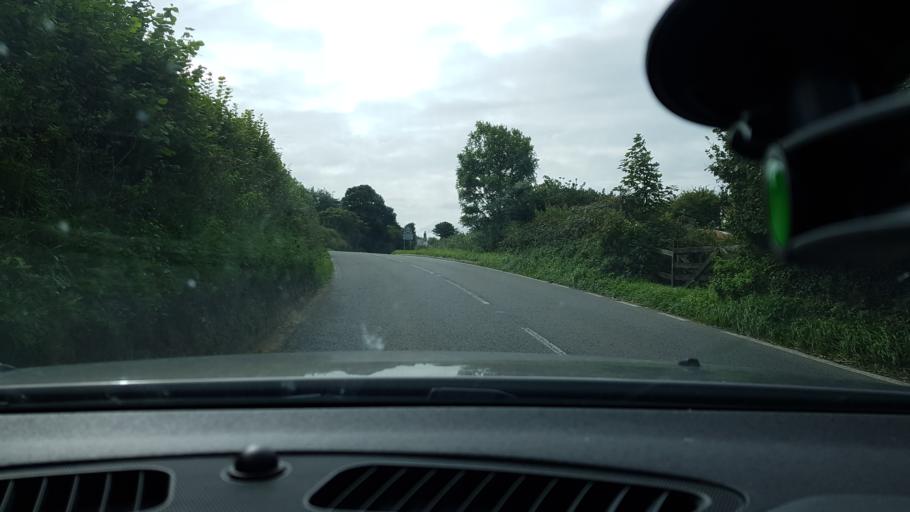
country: GB
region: England
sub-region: Cornwall
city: Camelford
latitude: 50.6019
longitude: -4.6975
